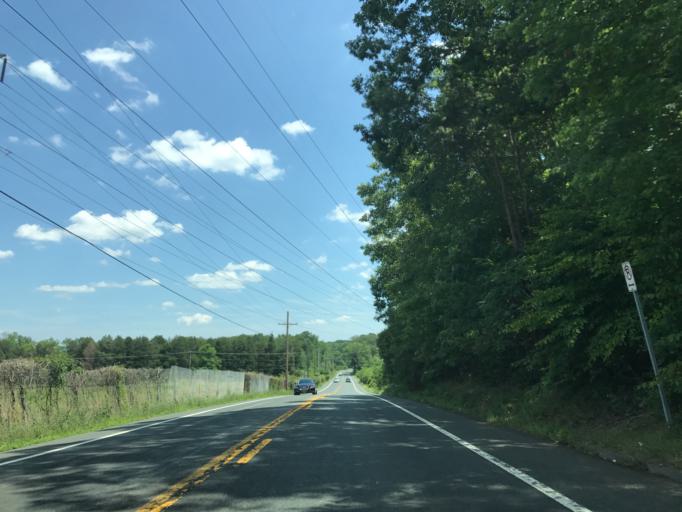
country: US
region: Maryland
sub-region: Anne Arundel County
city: Maryland City
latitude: 39.0458
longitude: -76.8034
